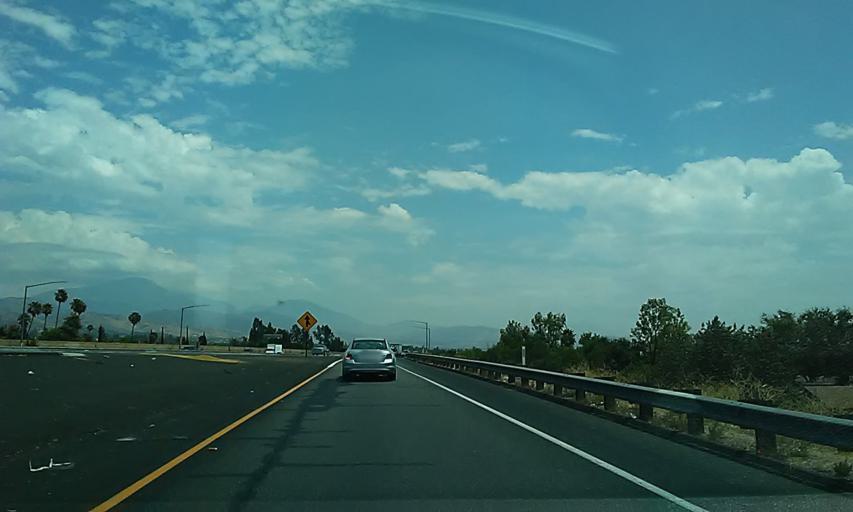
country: US
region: California
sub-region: San Bernardino County
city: Highland
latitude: 34.1341
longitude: -117.2327
